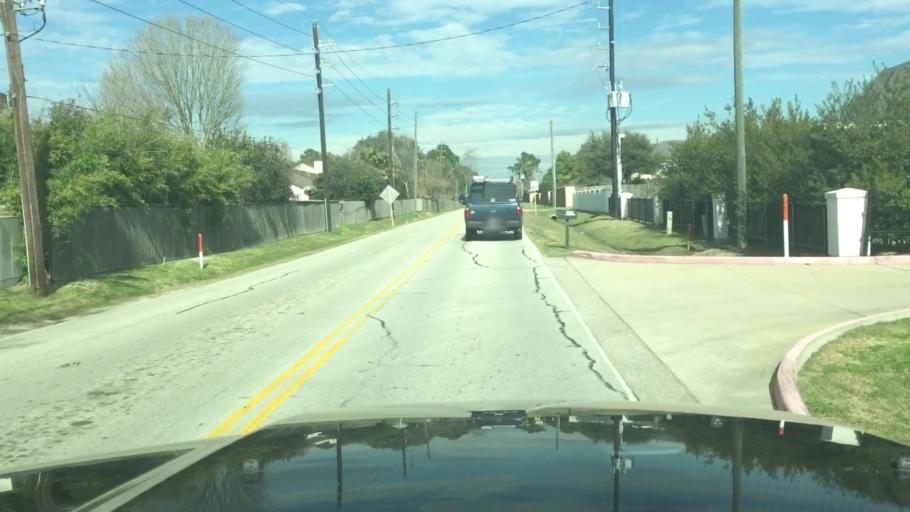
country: US
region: Texas
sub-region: Harris County
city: Oak Cliff Place
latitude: 29.8314
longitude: -95.6751
